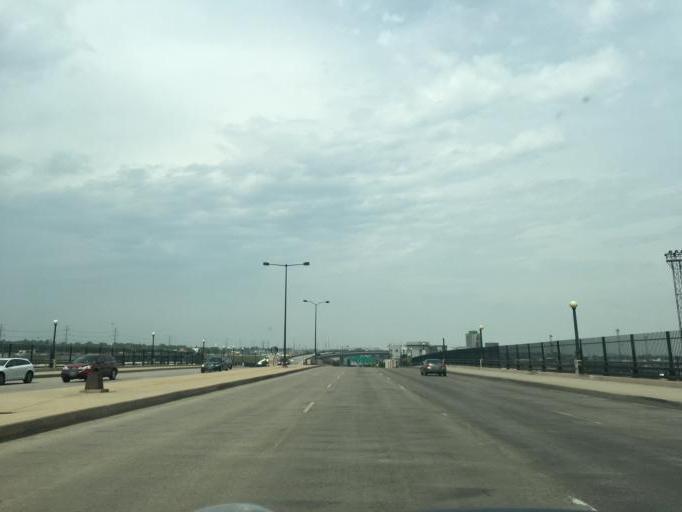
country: US
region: Colorado
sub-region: Denver County
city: Denver
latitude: 39.7614
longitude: -104.9947
